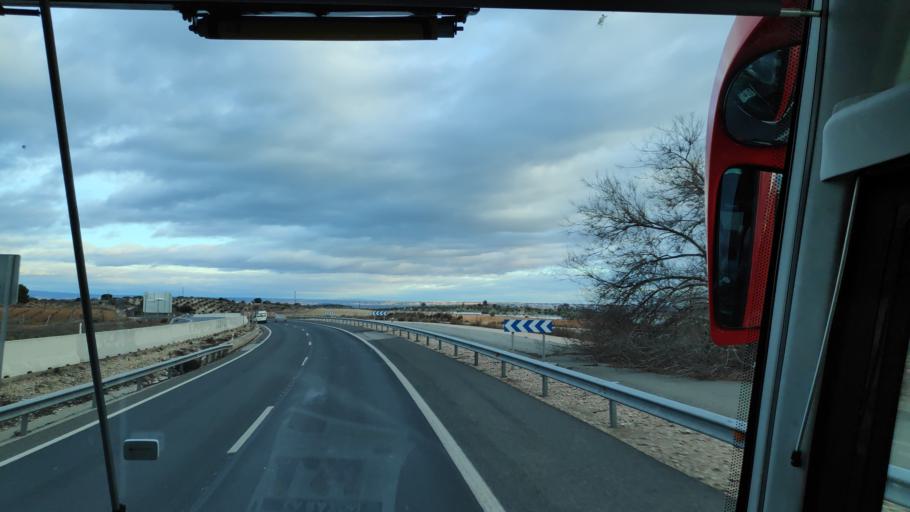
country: ES
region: Madrid
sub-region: Provincia de Madrid
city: Villarejo de Salvanes
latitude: 40.1572
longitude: -3.2589
